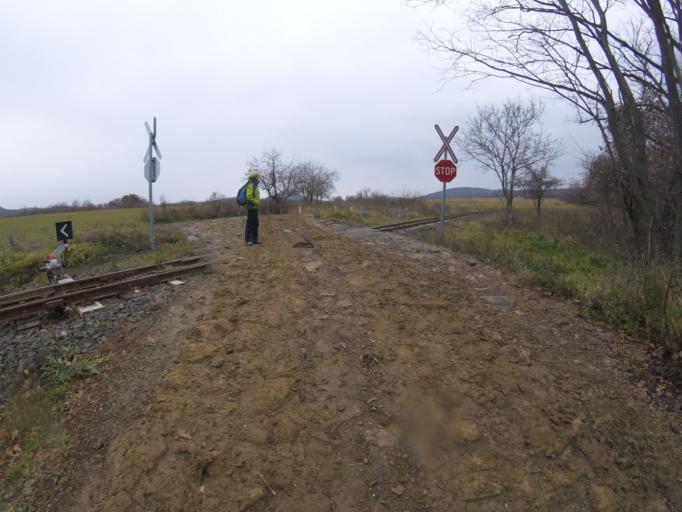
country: HU
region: Pest
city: Szob
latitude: 47.8677
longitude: 18.8643
